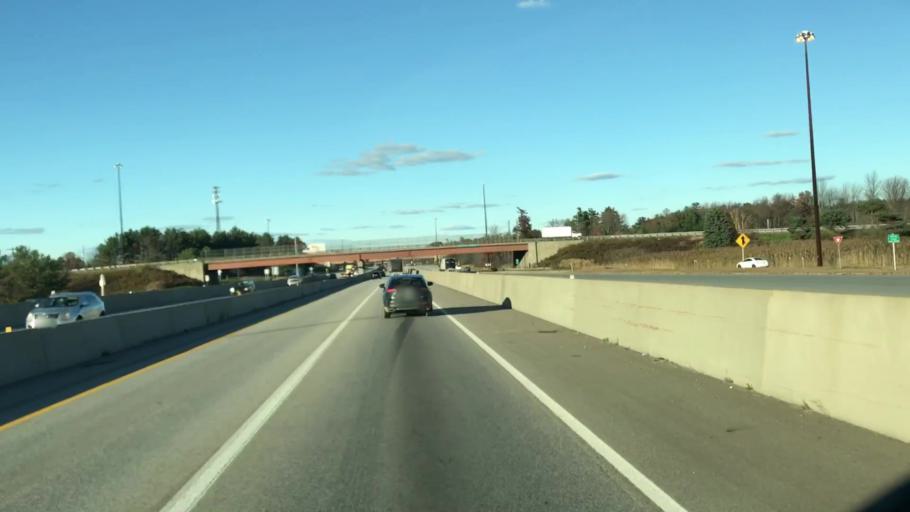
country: US
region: New Hampshire
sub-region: Rockingham County
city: North Hampton
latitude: 42.9633
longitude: -70.8561
